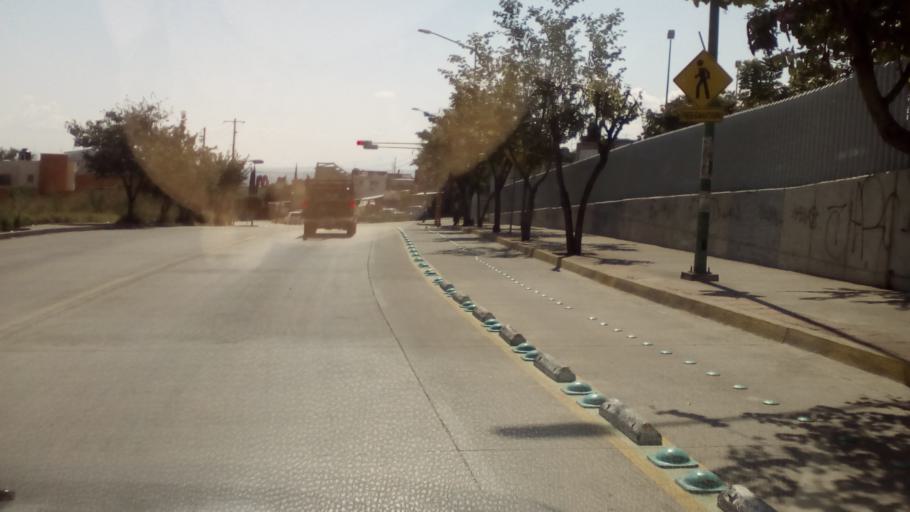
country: MX
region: Guanajuato
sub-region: Leon
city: Ejido la Joya
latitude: 21.1323
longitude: -101.7154
